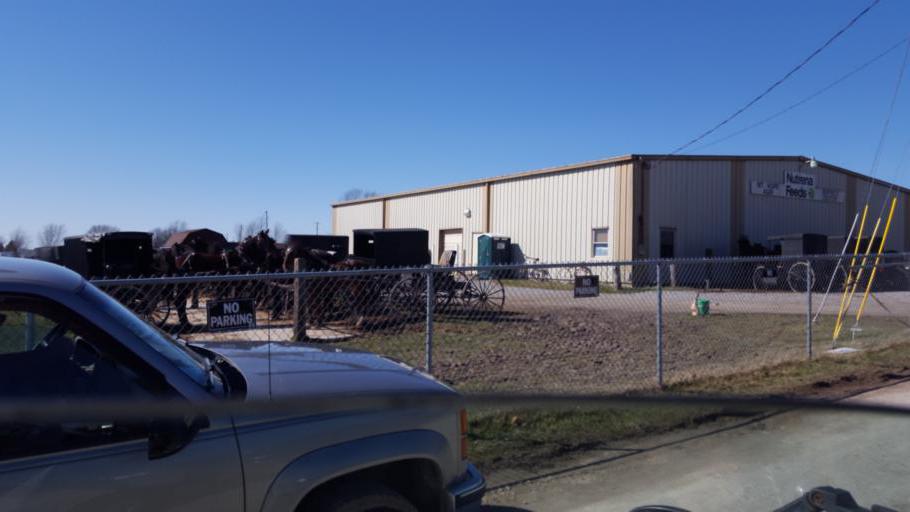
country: US
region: Ohio
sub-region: Wayne County
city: Apple Creek
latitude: 40.6234
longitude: -81.7872
